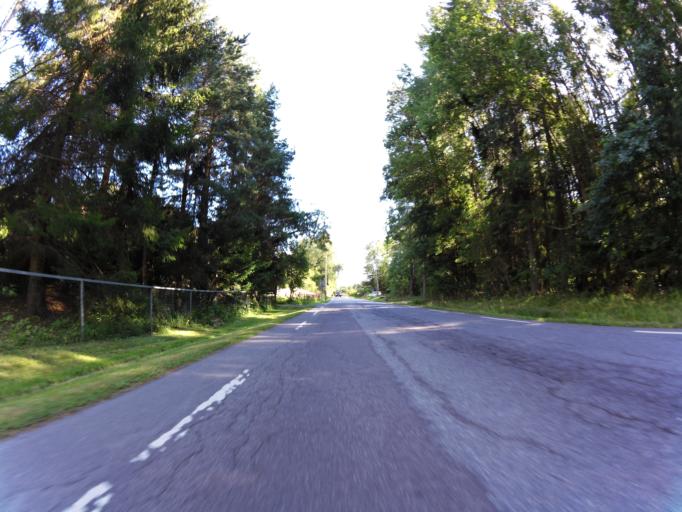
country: NO
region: Ostfold
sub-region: Fredrikstad
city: Fredrikstad
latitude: 59.1808
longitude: 10.8391
